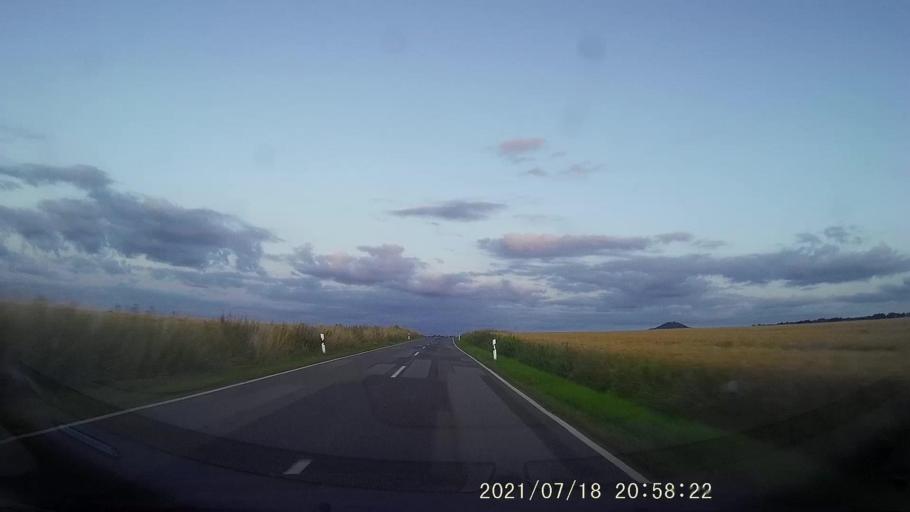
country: DE
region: Saxony
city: Konigshain
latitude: 51.1719
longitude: 14.9102
